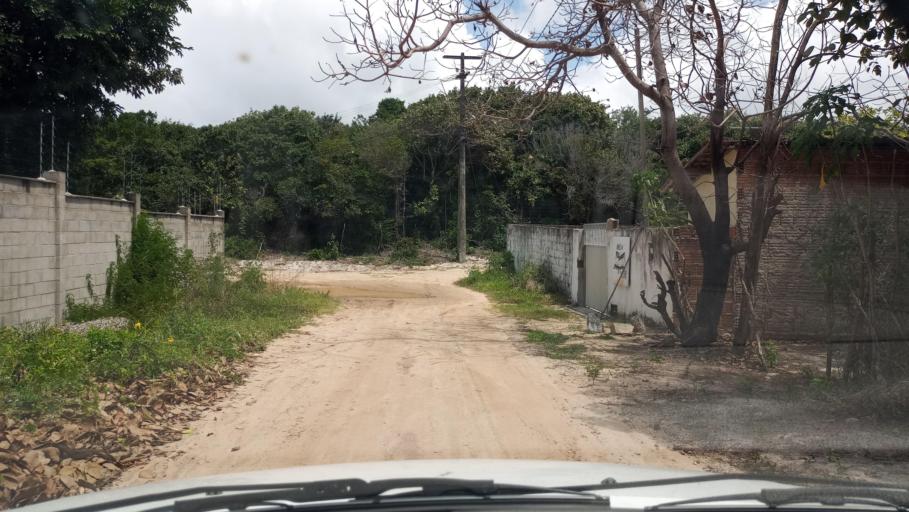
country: BR
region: Rio Grande do Norte
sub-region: Ares
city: Ares
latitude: -6.2460
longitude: -35.0445
